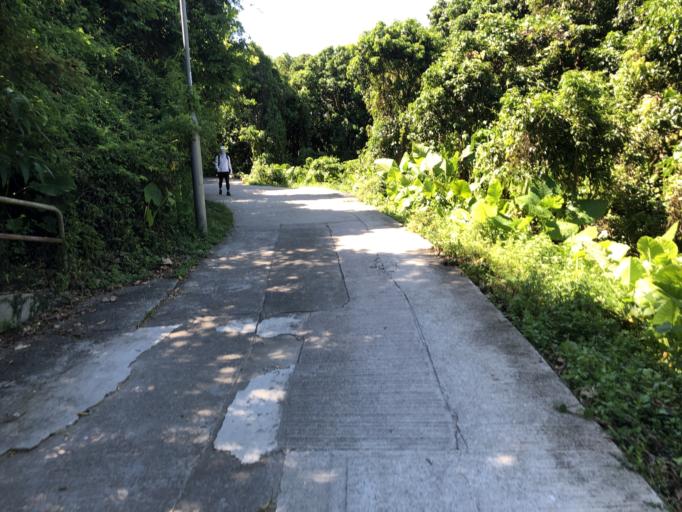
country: HK
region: Tuen Mun
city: Tuen Mun
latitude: 22.2963
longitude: 113.9701
